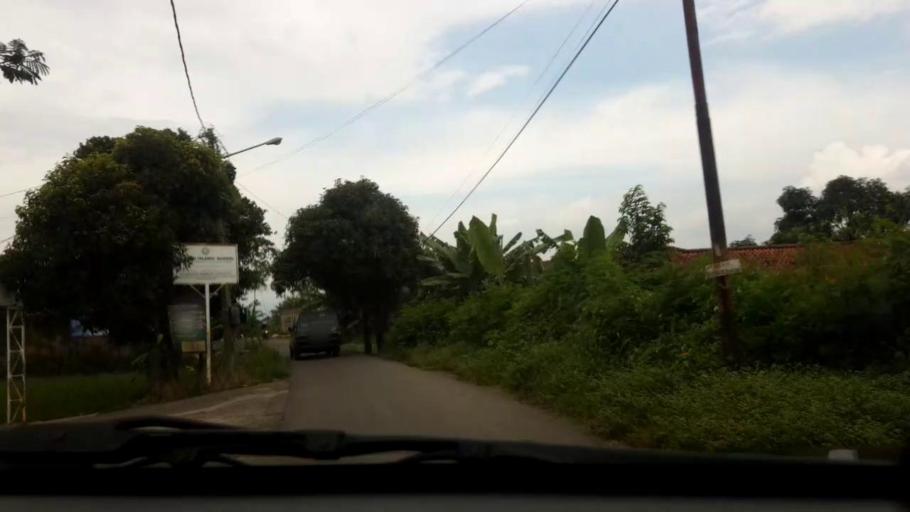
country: ID
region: West Java
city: Cileunyi
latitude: -6.9562
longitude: 107.7137
